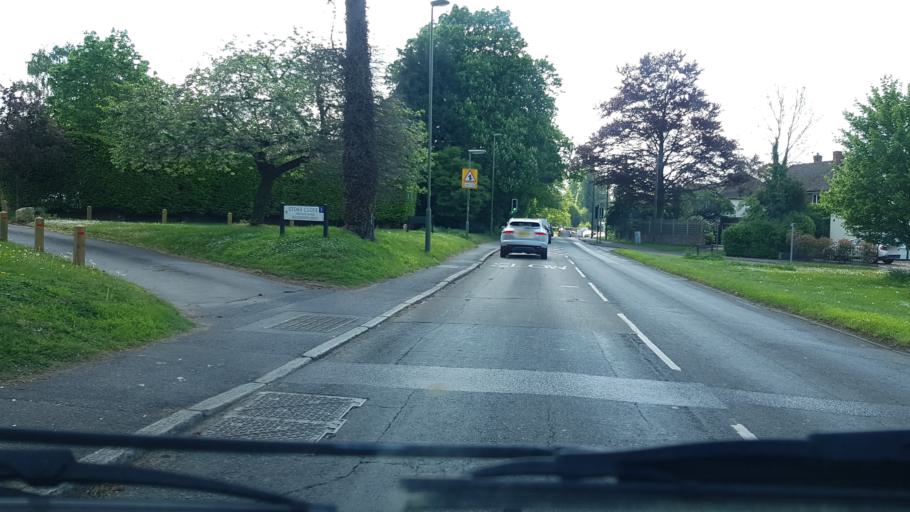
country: GB
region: England
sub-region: Surrey
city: Cobham
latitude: 51.3221
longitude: -0.3871
